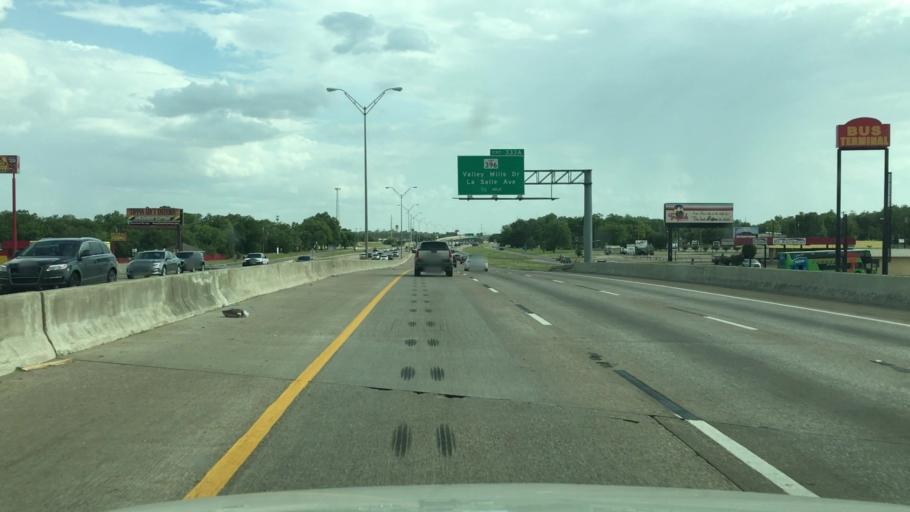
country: US
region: Texas
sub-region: McLennan County
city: Beverly
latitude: 31.5350
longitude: -97.1299
